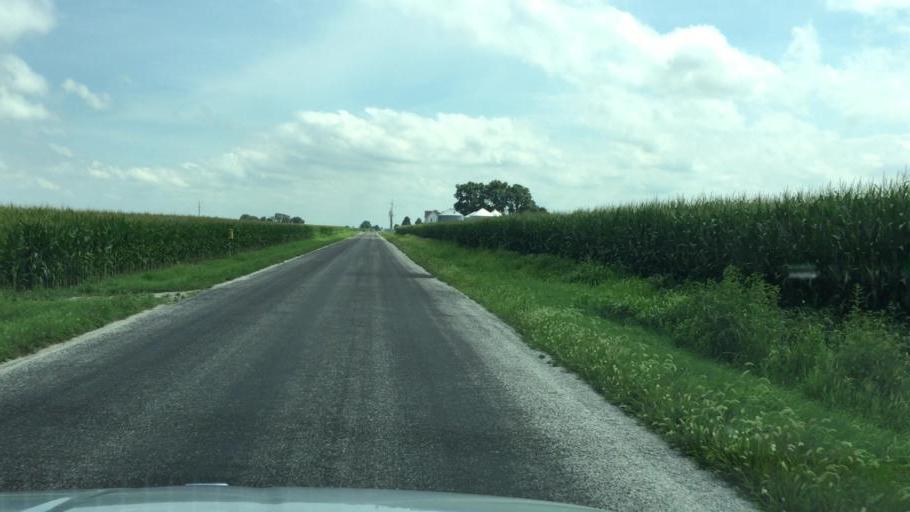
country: US
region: Illinois
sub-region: Hancock County
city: Carthage
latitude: 40.5247
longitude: -91.1771
